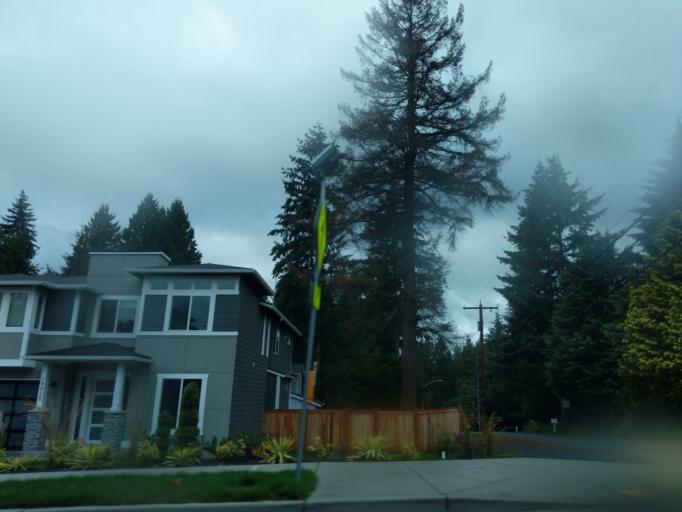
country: US
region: Washington
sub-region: King County
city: Bothell
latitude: 47.7727
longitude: -122.2069
